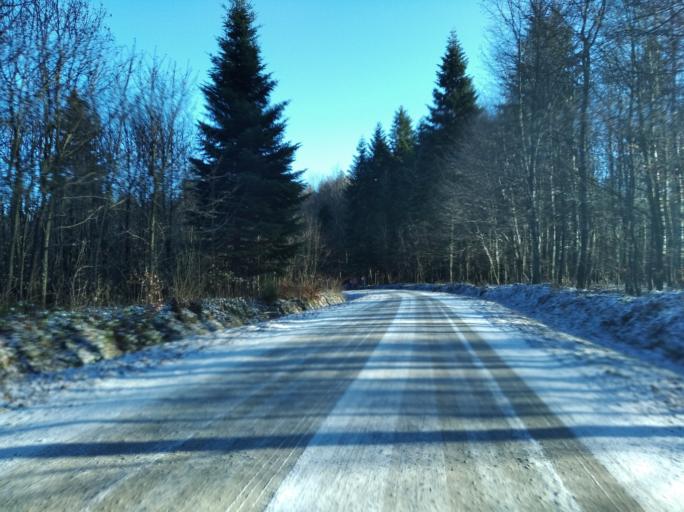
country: PL
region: Subcarpathian Voivodeship
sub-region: Powiat strzyzowski
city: Czudec
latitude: 49.9716
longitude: 21.7879
